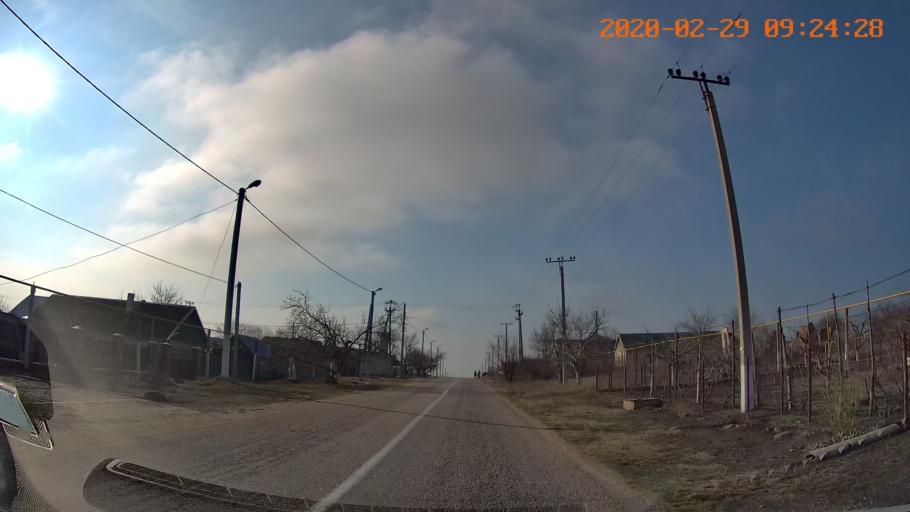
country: MD
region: Telenesti
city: Pervomaisc
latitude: 46.7158
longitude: 29.9585
